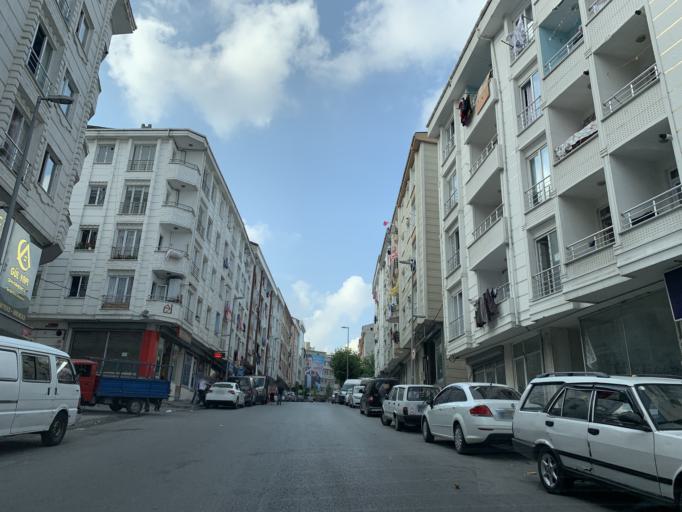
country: TR
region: Istanbul
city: Esenyurt
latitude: 41.0303
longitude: 28.6747
